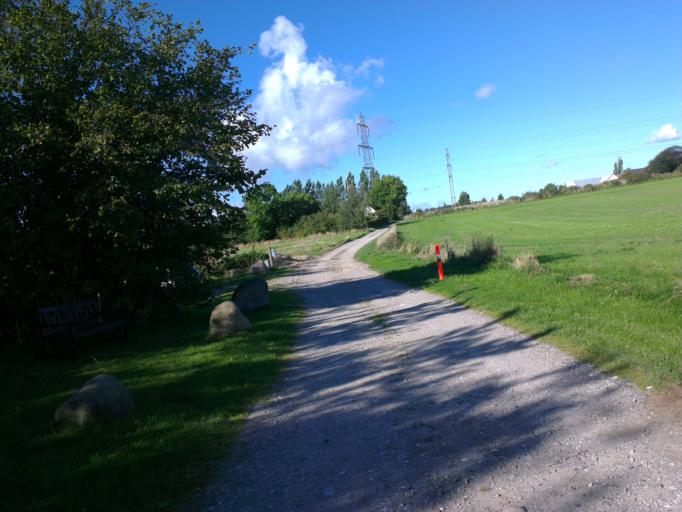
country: DK
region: Capital Region
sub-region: Frederikssund Kommune
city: Frederikssund
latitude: 55.7951
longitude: 12.0316
